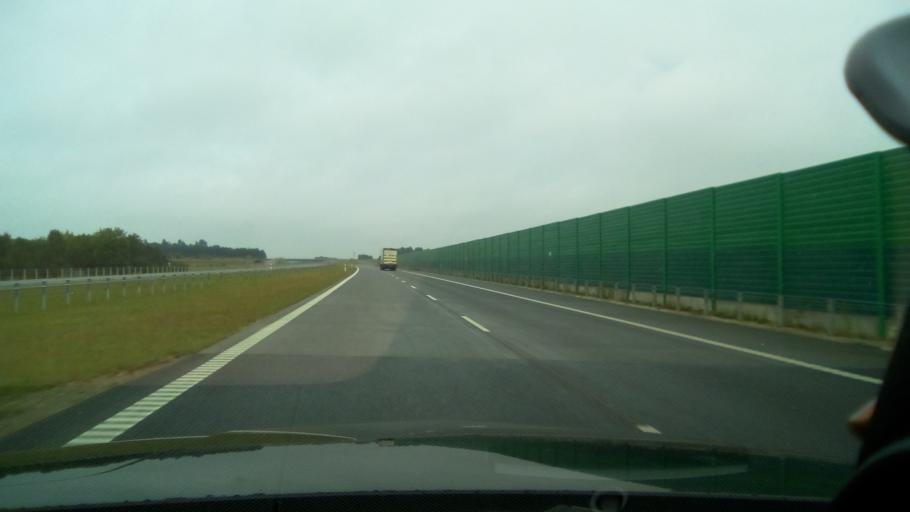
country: PL
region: Silesian Voivodeship
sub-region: Powiat klobucki
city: Kamyk
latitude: 50.8709
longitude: 19.0902
